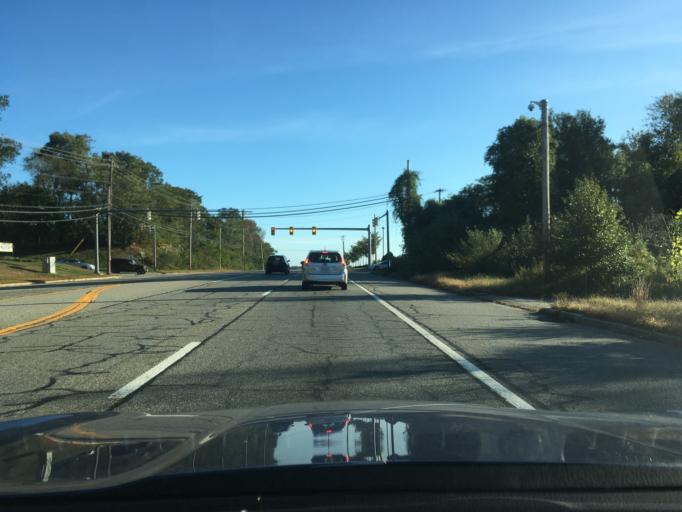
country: US
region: Rhode Island
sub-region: Kent County
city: West Warwick
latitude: 41.6781
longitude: -71.5002
